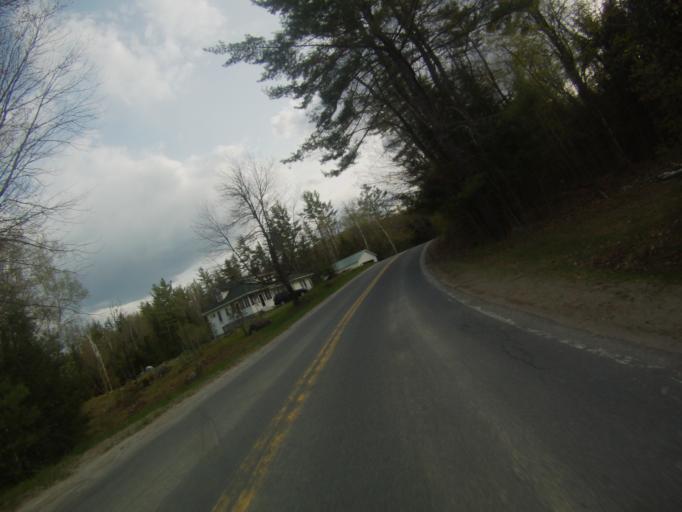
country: US
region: New York
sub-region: Warren County
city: Warrensburg
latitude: 43.8302
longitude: -73.8988
